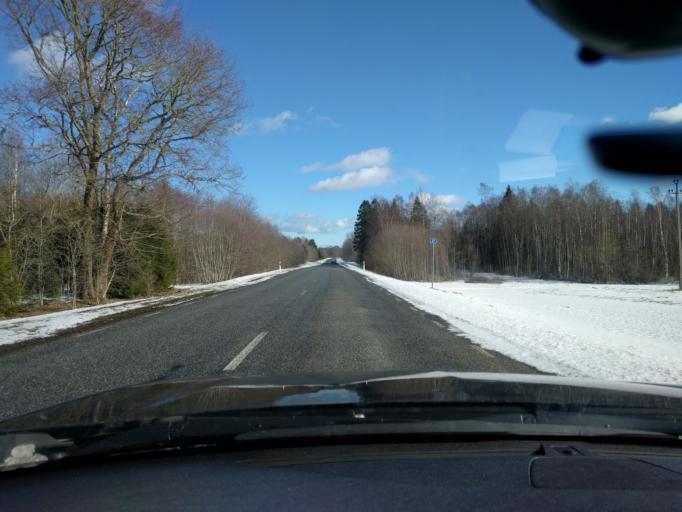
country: EE
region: Harju
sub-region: Raasiku vald
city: Raasiku
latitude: 59.4087
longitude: 25.2172
